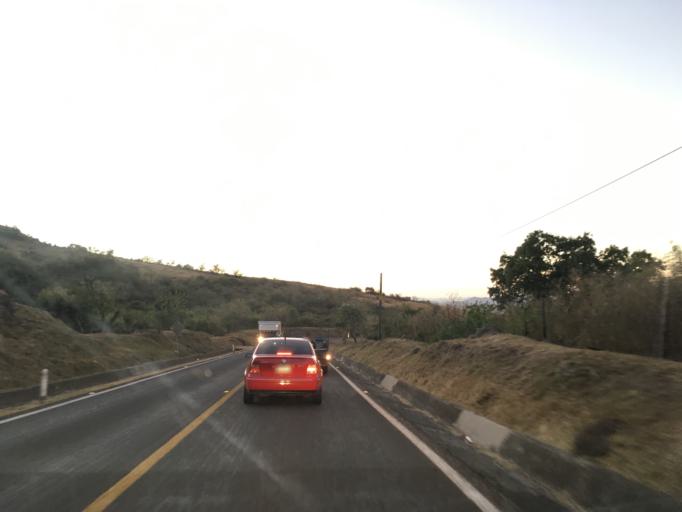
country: MX
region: Michoacan
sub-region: Zinapecuaro
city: Santa Clara del Tule
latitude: 19.8116
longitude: -100.8224
